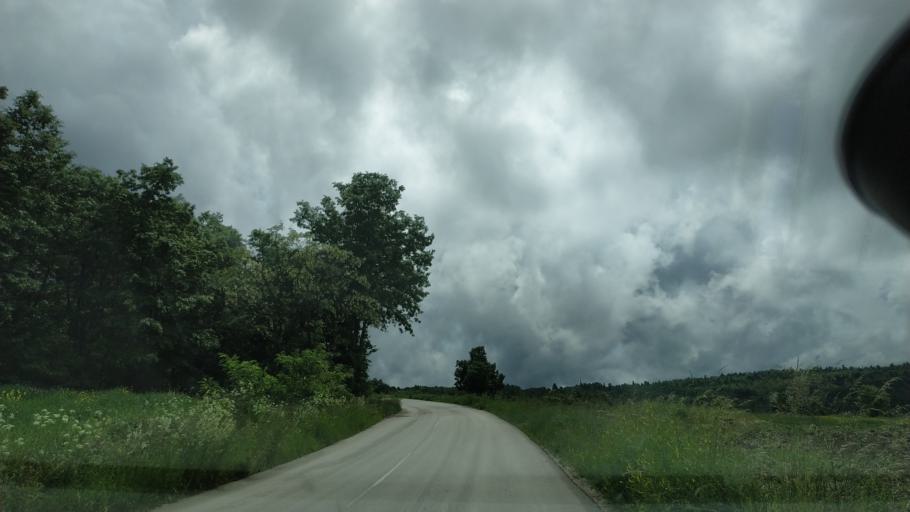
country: RS
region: Central Serbia
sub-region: Zajecarski Okrug
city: Soko Banja
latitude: 43.6873
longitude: 21.9306
